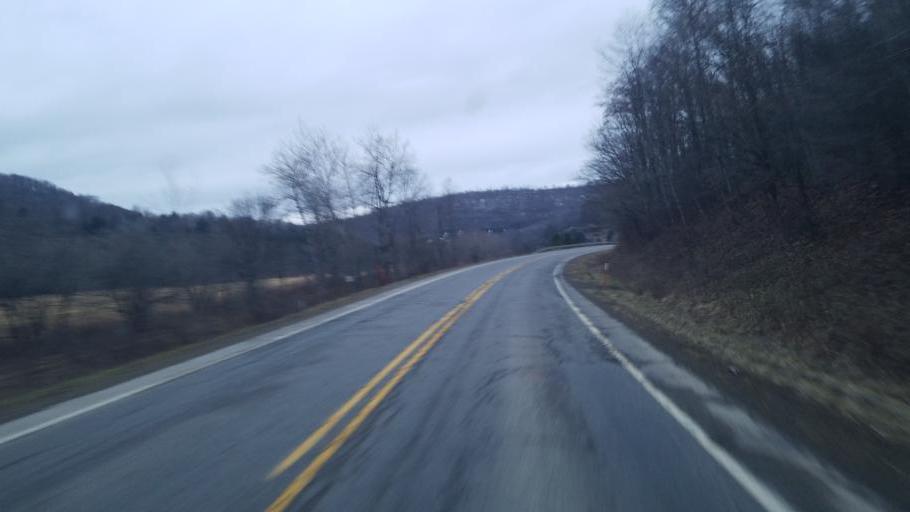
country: US
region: Pennsylvania
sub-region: Potter County
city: Coudersport
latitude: 41.8348
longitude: -77.9322
